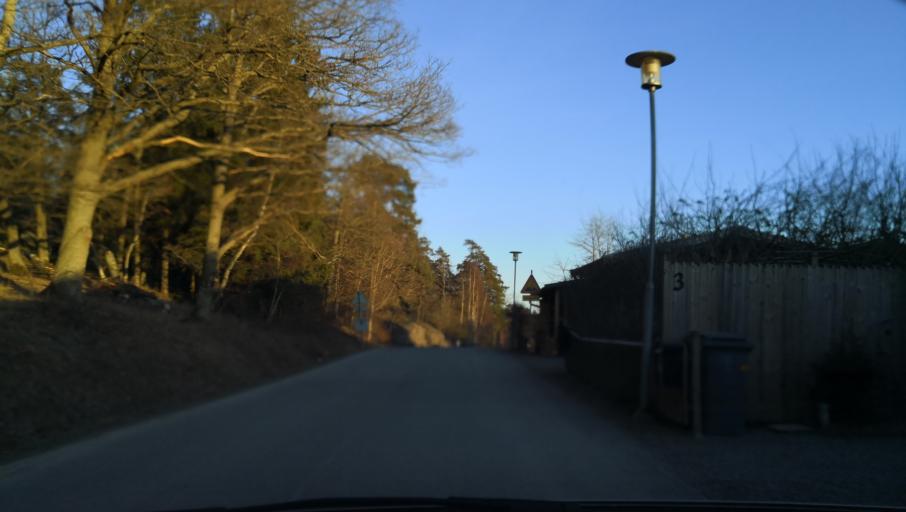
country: SE
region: Stockholm
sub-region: Varmdo Kommun
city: Gustavsberg
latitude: 59.3313
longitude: 18.4065
